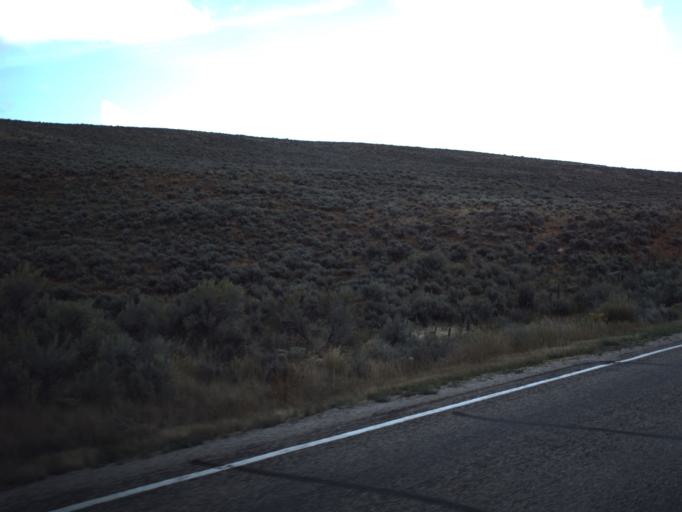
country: US
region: Utah
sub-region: Rich County
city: Randolph
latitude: 41.7936
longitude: -111.2231
